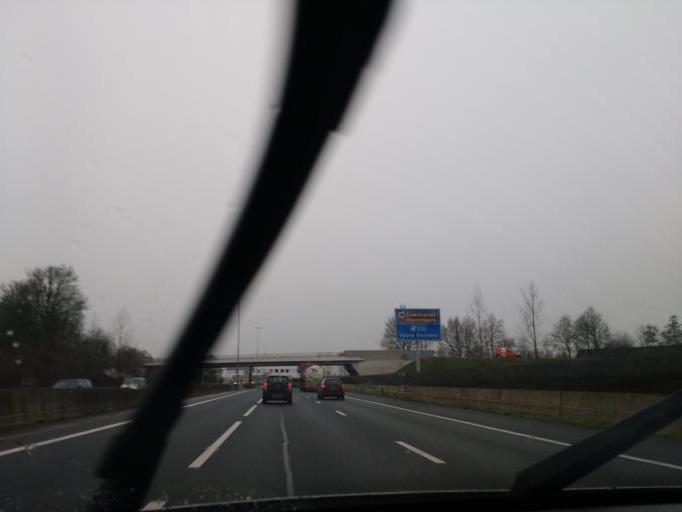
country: NL
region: Gelderland
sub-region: Gemeente Ede
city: Ederveen
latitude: 52.0326
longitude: 5.5955
